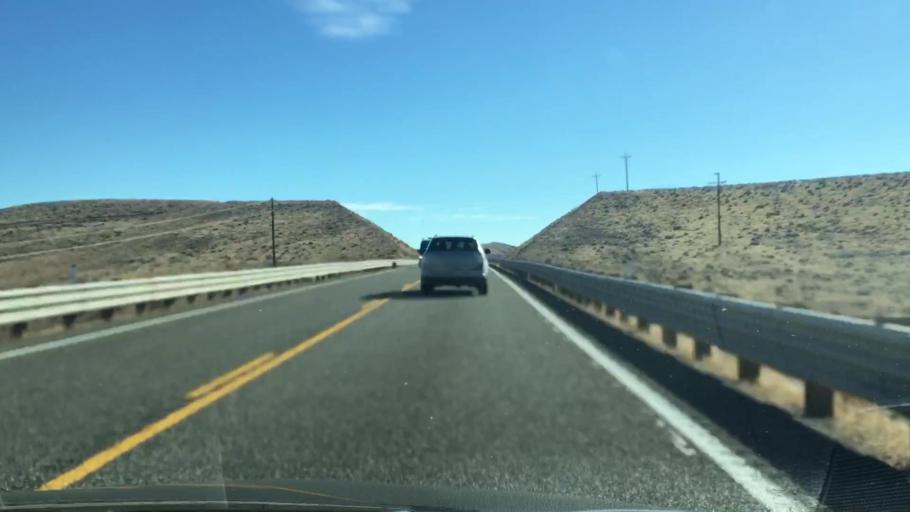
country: US
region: Nevada
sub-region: Lyon County
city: Silver Springs
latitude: 39.2161
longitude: -119.2210
